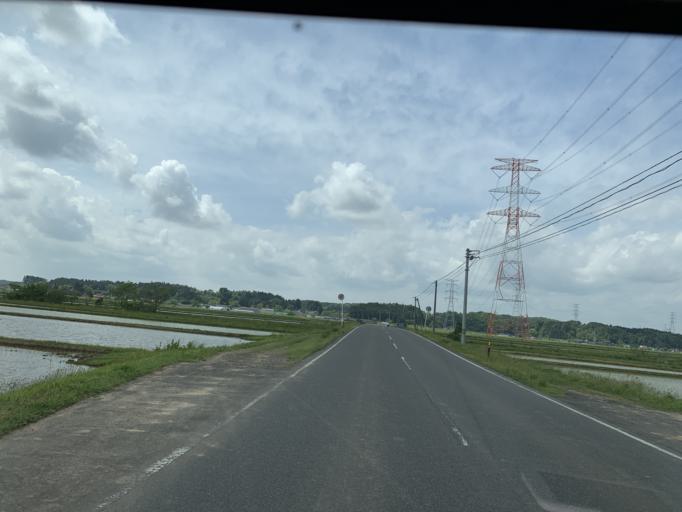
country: JP
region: Iwate
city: Ichinoseki
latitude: 38.7988
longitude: 141.0075
